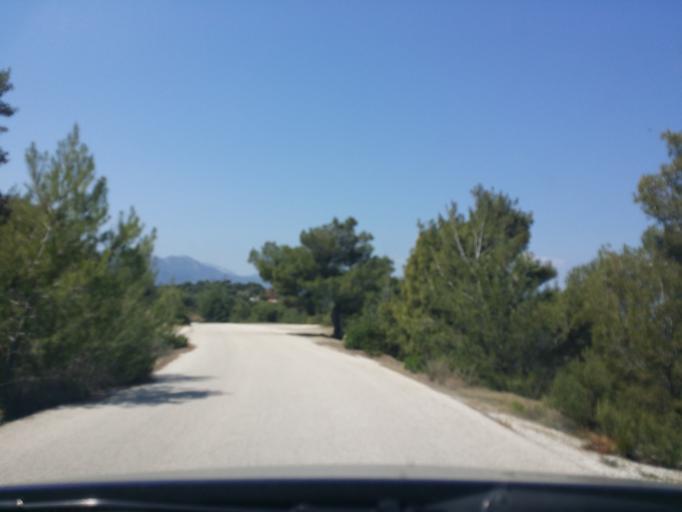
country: GR
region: Attica
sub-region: Nomos Piraios
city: Poros
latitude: 37.5226
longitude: 23.4361
